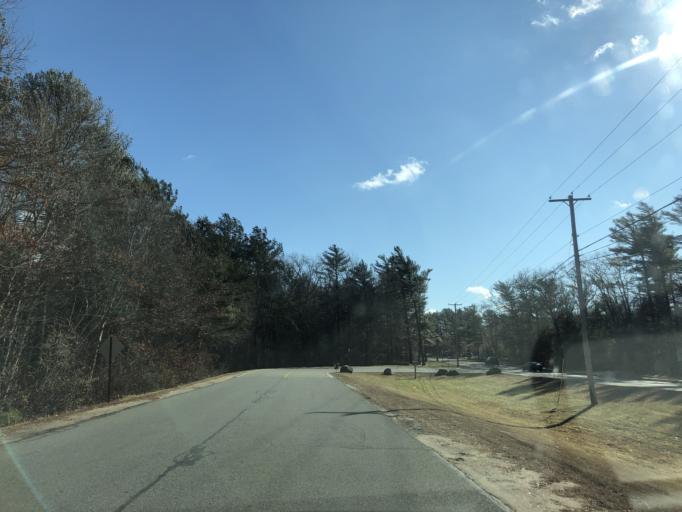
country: US
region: Massachusetts
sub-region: Plymouth County
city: Mattapoisett Center
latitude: 41.6736
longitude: -70.8193
